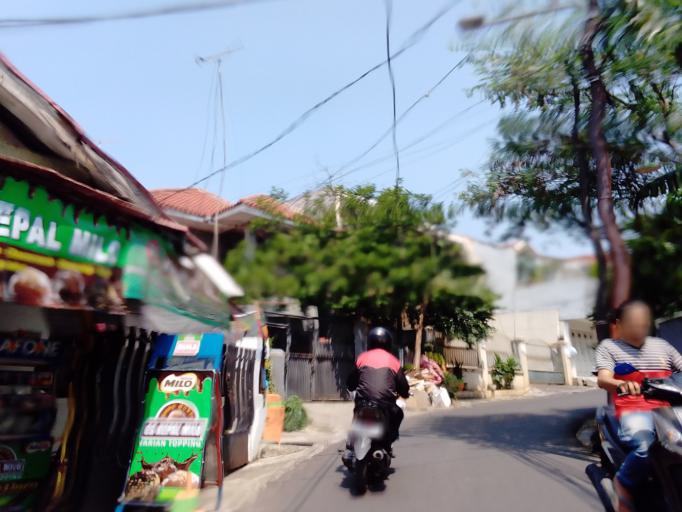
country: ID
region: Jakarta Raya
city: Jakarta
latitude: -6.2618
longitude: 106.8019
